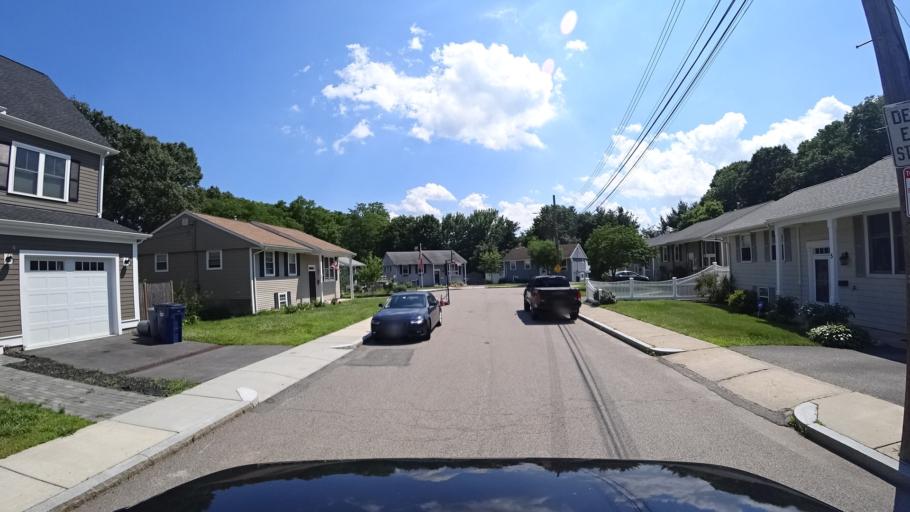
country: US
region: Massachusetts
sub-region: Norfolk County
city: Dedham
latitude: 42.2690
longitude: -71.1669
